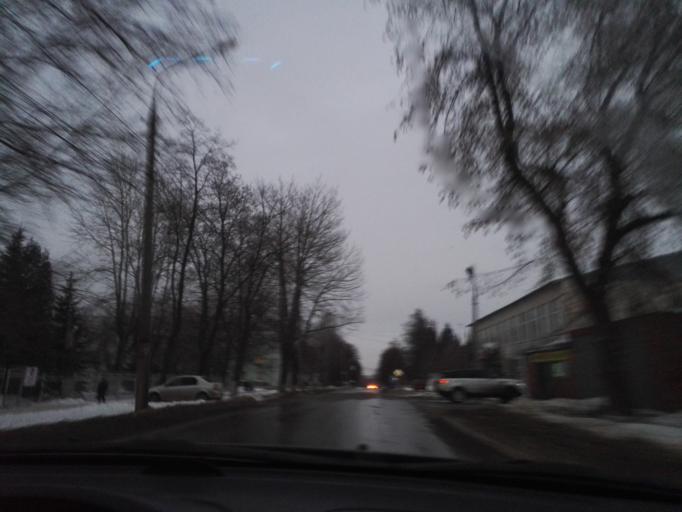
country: RU
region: Tula
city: Novomoskovsk
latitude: 54.0047
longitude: 38.3030
